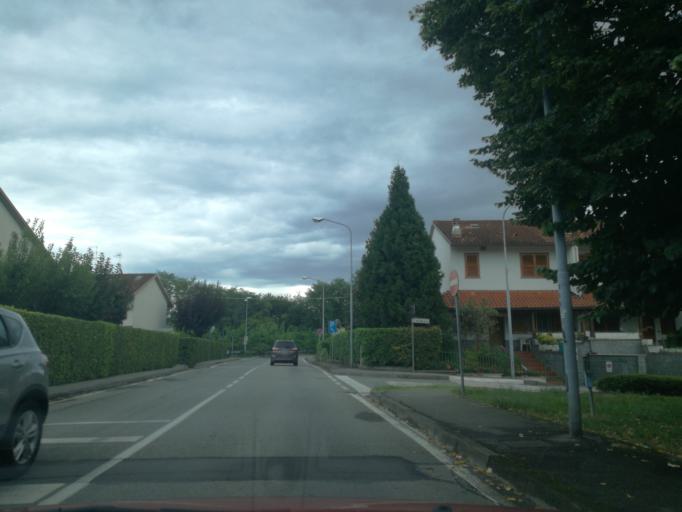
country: IT
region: Lombardy
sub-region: Provincia di Monza e Brianza
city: Ornago
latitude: 45.6040
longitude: 9.4208
